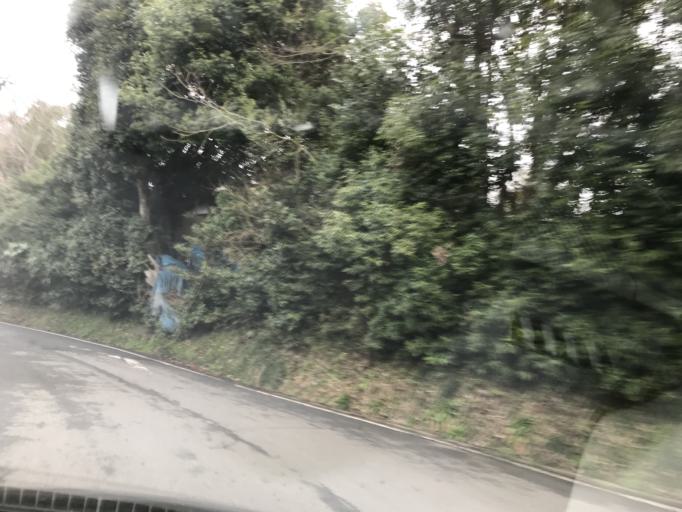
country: JP
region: Chiba
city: Sawara
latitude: 35.8509
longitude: 140.5314
